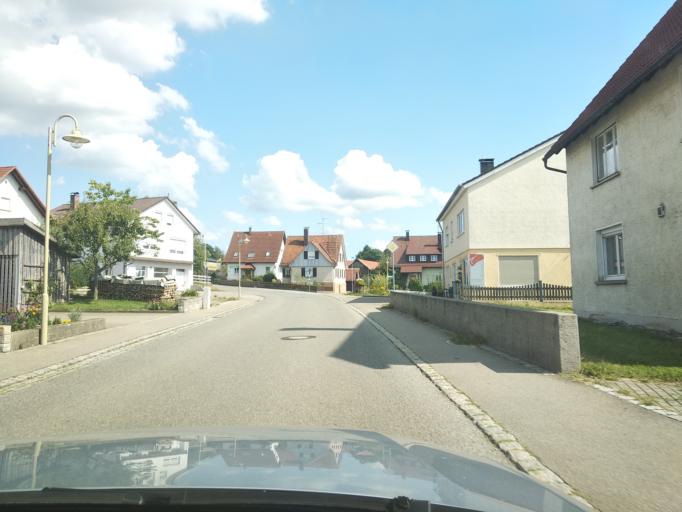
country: DE
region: Baden-Wuerttemberg
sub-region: Tuebingen Region
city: Bad Wurzach
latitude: 47.8899
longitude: 9.9732
